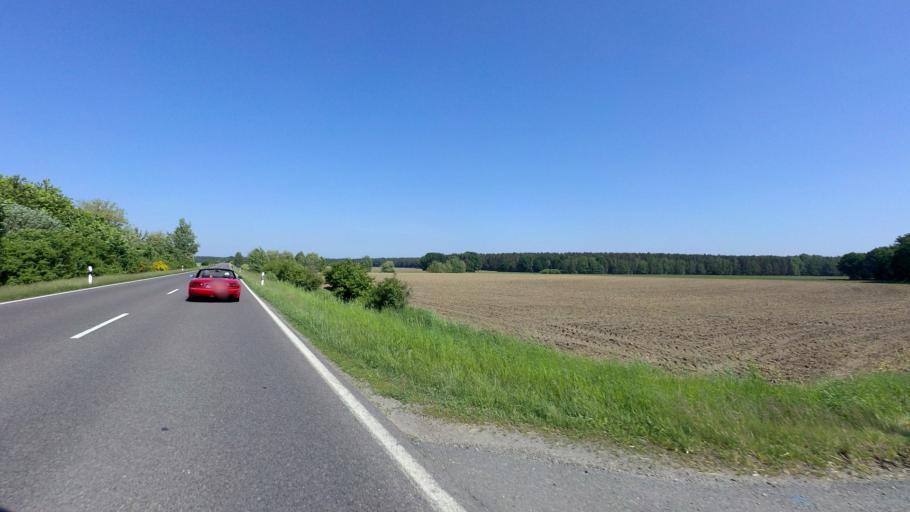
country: DE
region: Saxony
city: Bernsdorf
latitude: 51.3255
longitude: 14.0805
